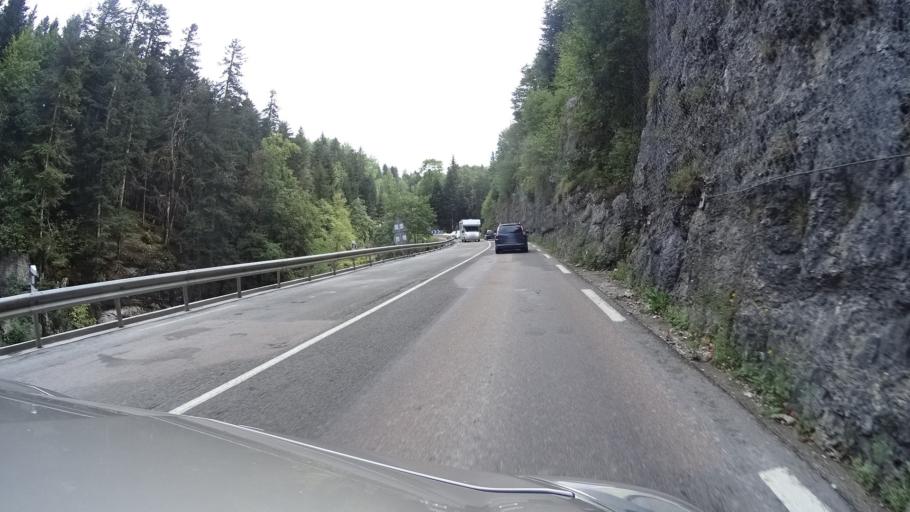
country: FR
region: Franche-Comte
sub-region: Departement du Jura
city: Champagnole
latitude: 46.6646
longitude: 5.9465
